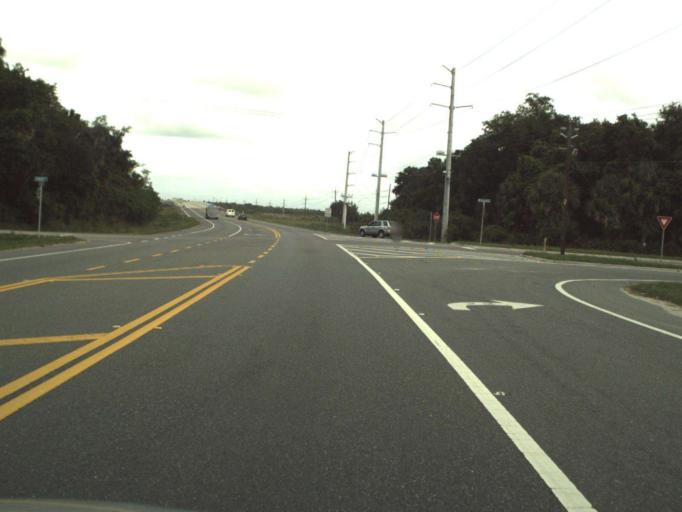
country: US
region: Florida
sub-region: Seminole County
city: Midway
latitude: 28.7802
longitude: -81.1674
